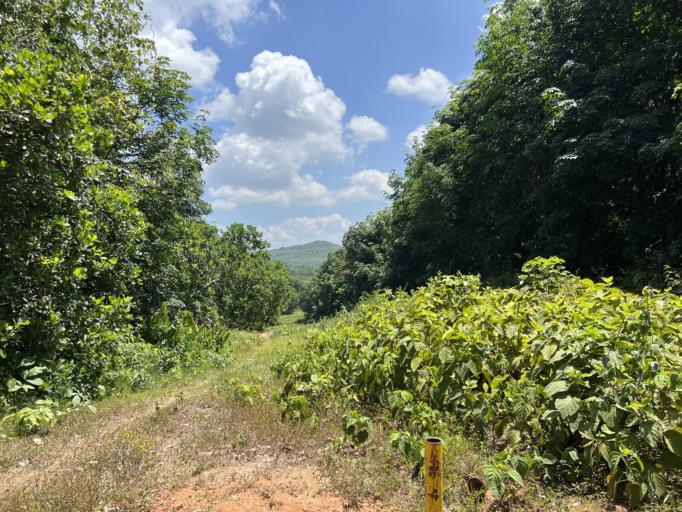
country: MM
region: Tanintharyi
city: Dawei
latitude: 14.5868
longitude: 97.9359
